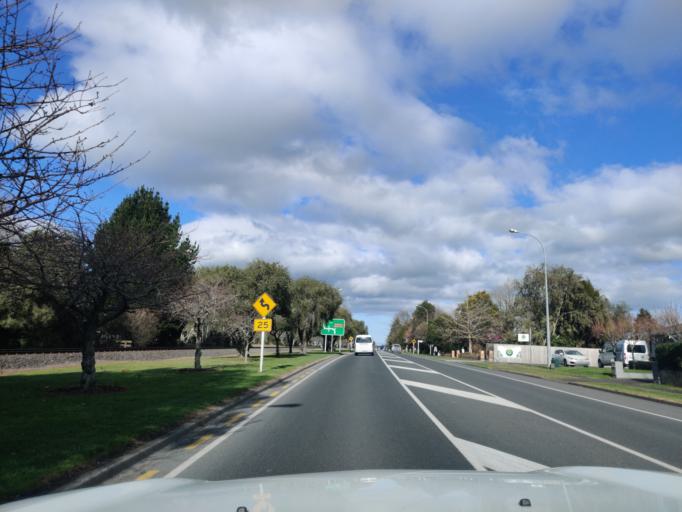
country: NZ
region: Waikato
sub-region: Matamata-Piako District
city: Matamata
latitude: -37.8232
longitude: 175.7708
